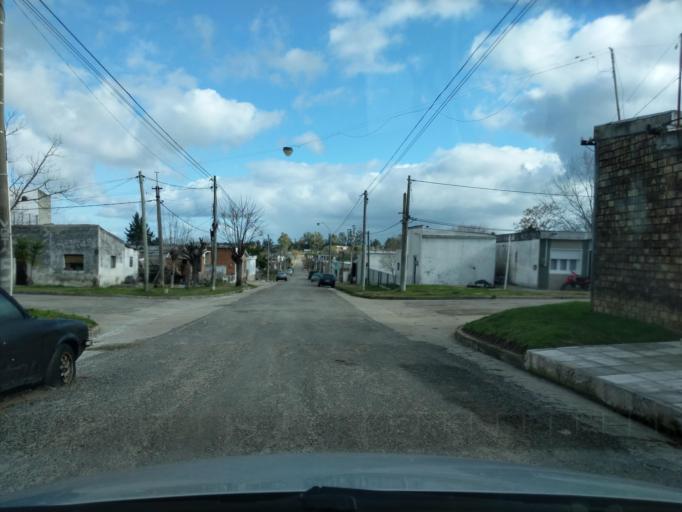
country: UY
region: Florida
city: Florida
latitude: -34.1047
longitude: -56.2182
